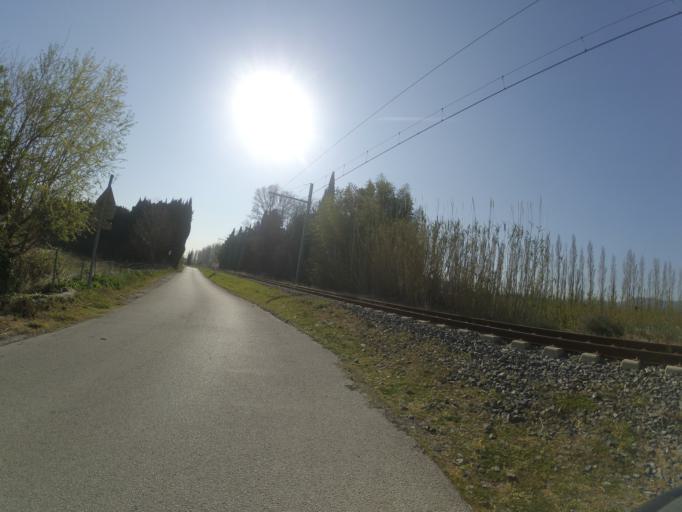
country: FR
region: Languedoc-Roussillon
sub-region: Departement des Pyrenees-Orientales
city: Millas
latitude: 42.6860
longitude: 2.7021
